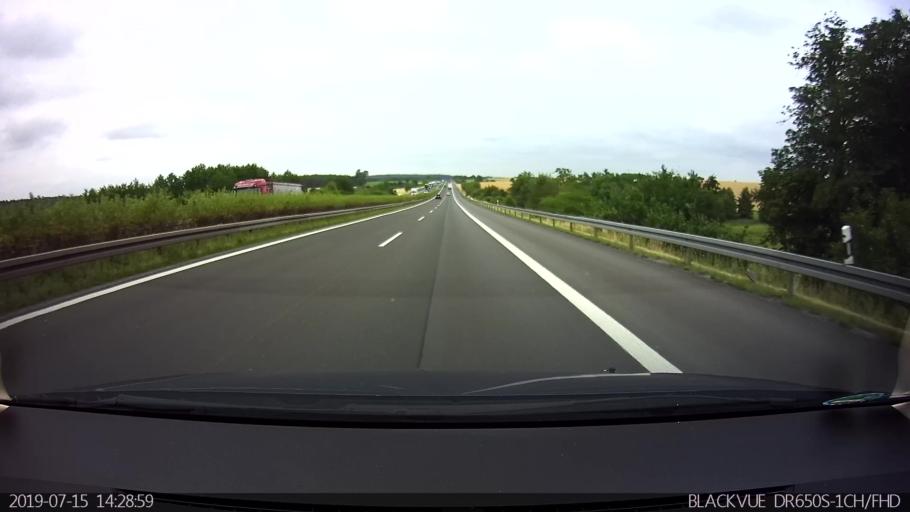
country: DE
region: Saxony
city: Wachau
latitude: 51.1713
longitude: 13.8824
